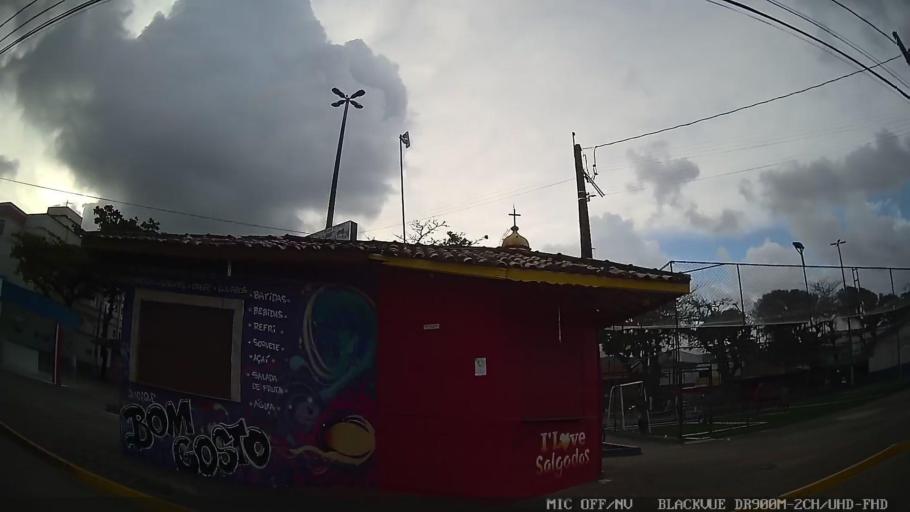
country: BR
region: Sao Paulo
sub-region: Itanhaem
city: Itanhaem
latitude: -24.1631
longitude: -46.7524
